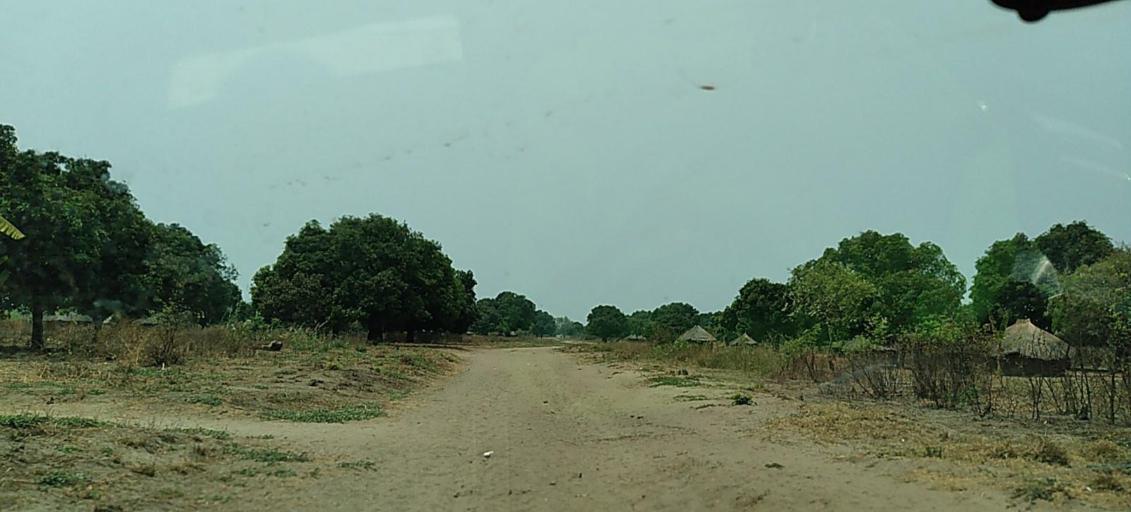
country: ZM
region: Western
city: Lukulu
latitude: -14.1586
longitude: 23.3126
